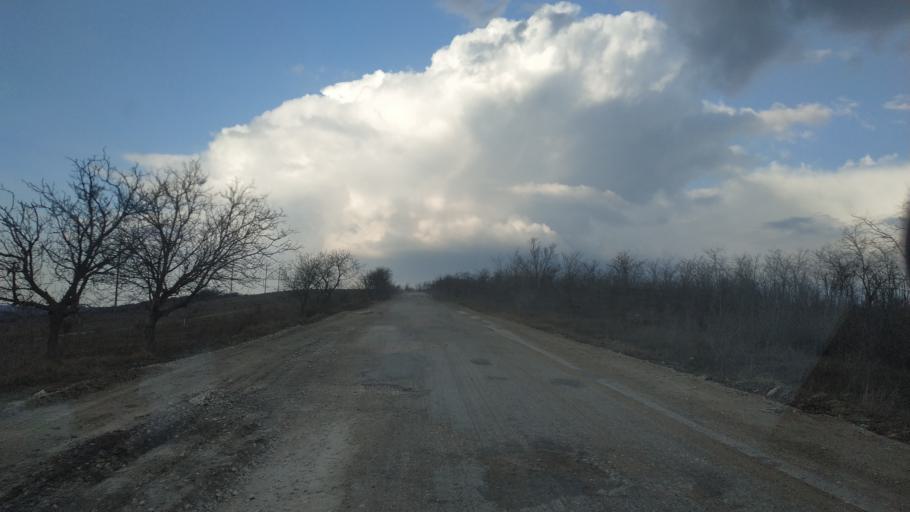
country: MD
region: Anenii Noi
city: Anenii Noi
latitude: 46.9873
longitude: 29.2843
